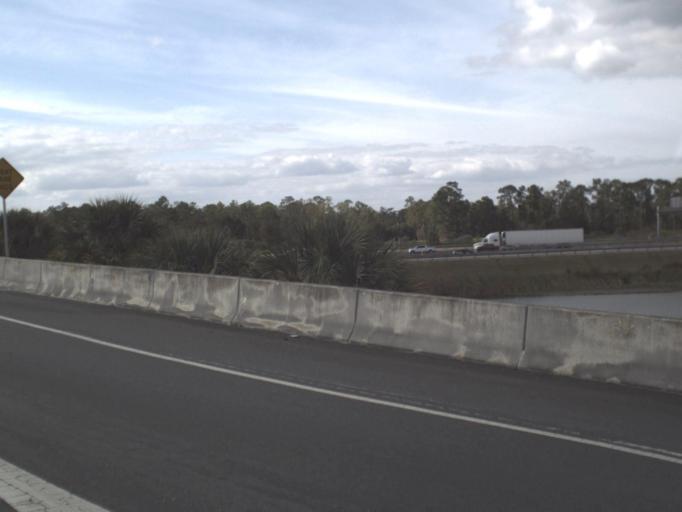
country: US
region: Florida
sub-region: Osceola County
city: Celebration
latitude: 28.3457
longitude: -81.5307
